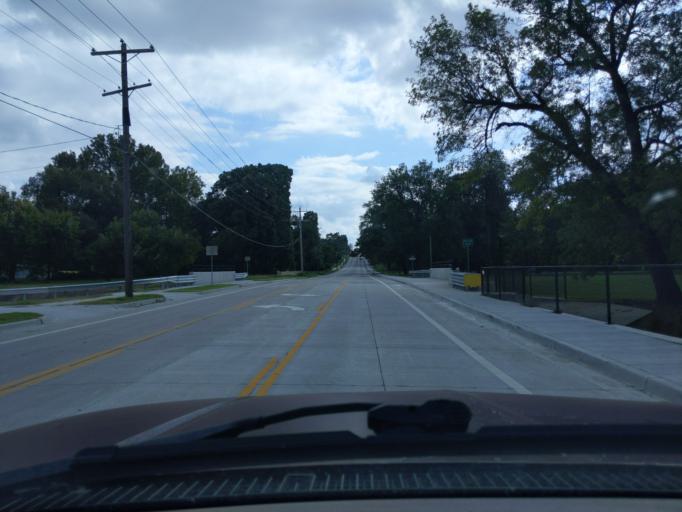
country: US
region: Oklahoma
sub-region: Tulsa County
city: Tulsa
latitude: 36.1029
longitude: -96.0116
